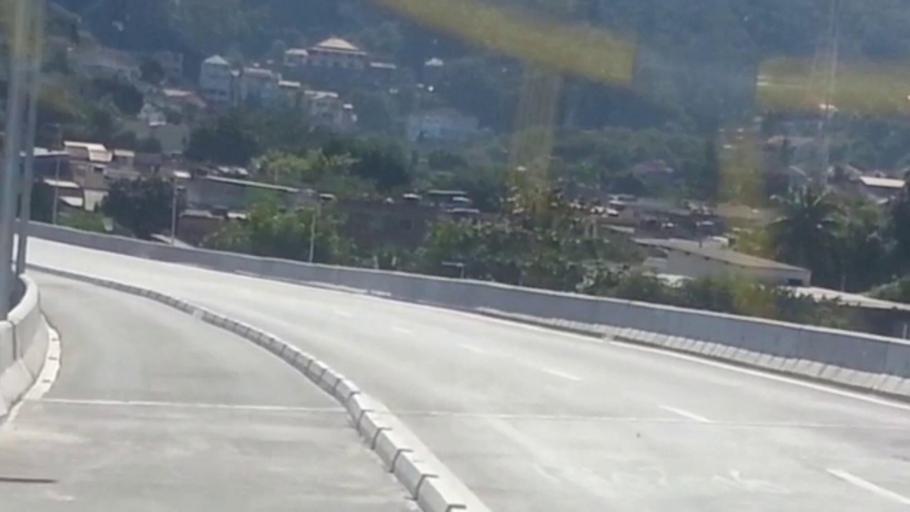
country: BR
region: Rio de Janeiro
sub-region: Nilopolis
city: Nilopolis
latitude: -22.9184
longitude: -43.3964
